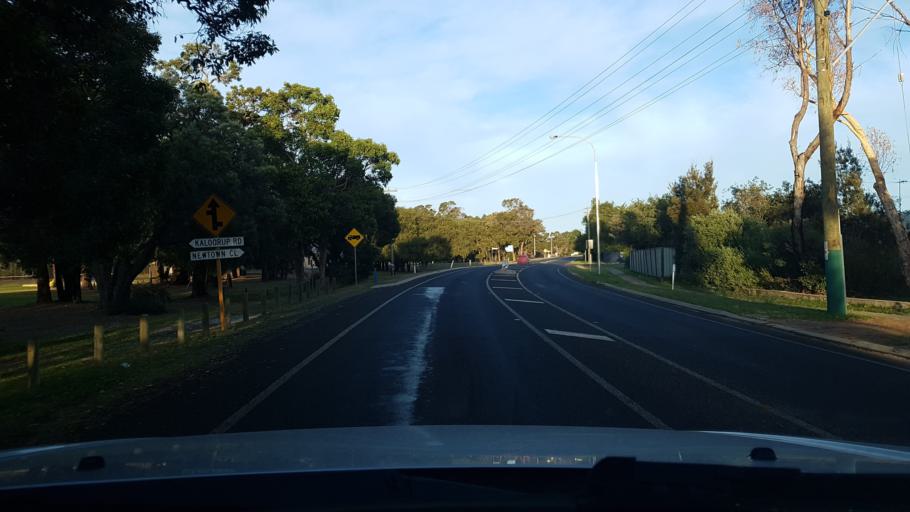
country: AU
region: Western Australia
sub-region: Busselton
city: Vasse
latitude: -33.6769
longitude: 115.2499
